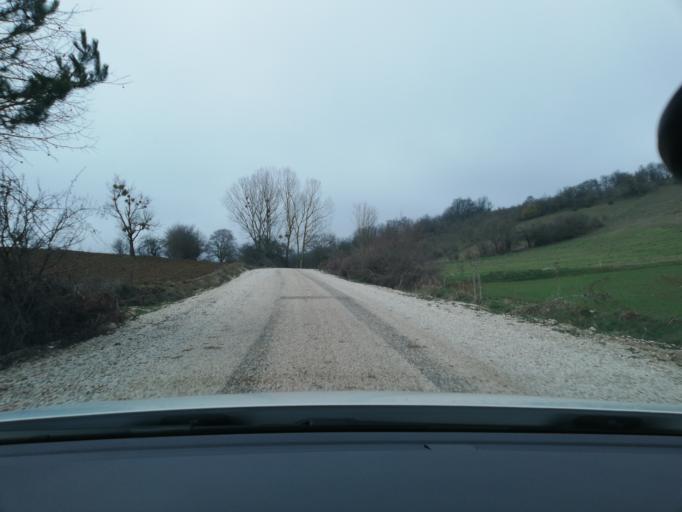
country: TR
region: Bolu
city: Bolu
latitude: 40.6610
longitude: 31.4683
